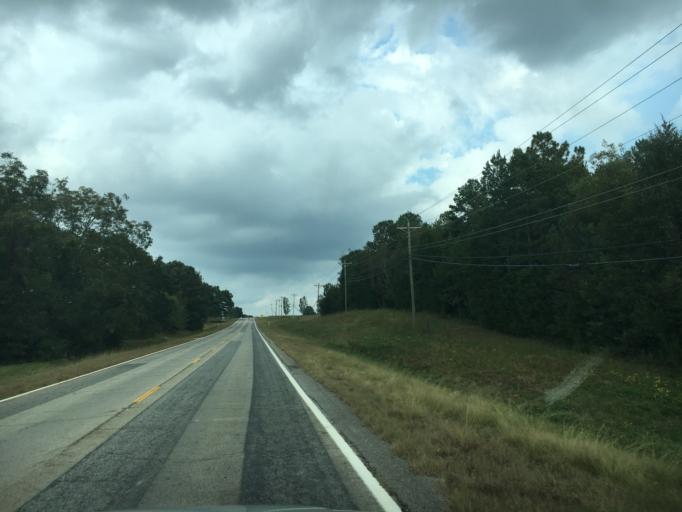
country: US
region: Georgia
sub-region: Hart County
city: Hartwell
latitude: 34.3917
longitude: -82.9383
